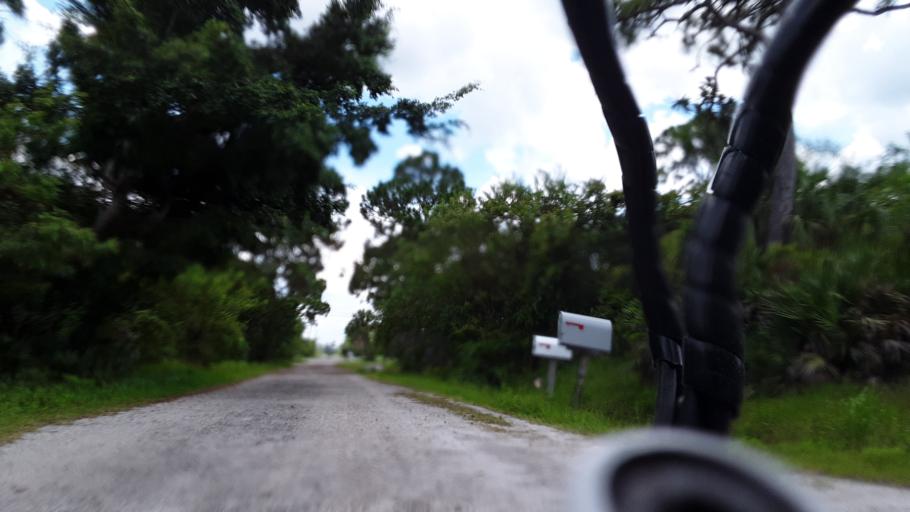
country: US
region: Florida
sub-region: Brevard County
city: Malabar
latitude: 27.9845
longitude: -80.5774
